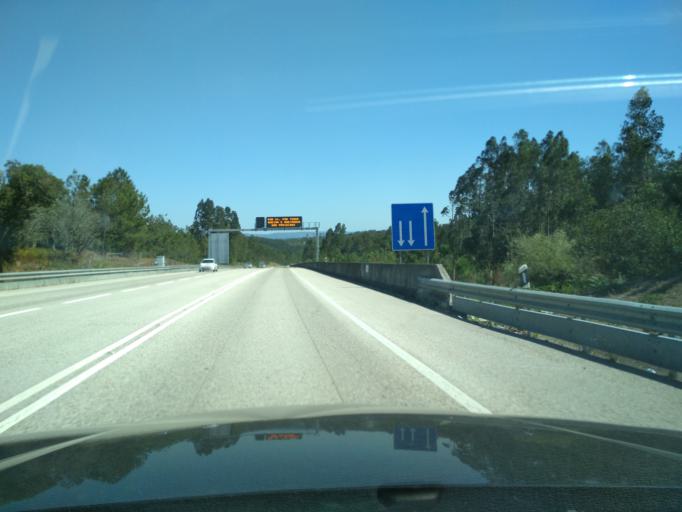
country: PT
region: Leiria
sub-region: Pombal
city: Lourical
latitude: 39.9887
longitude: -8.7784
